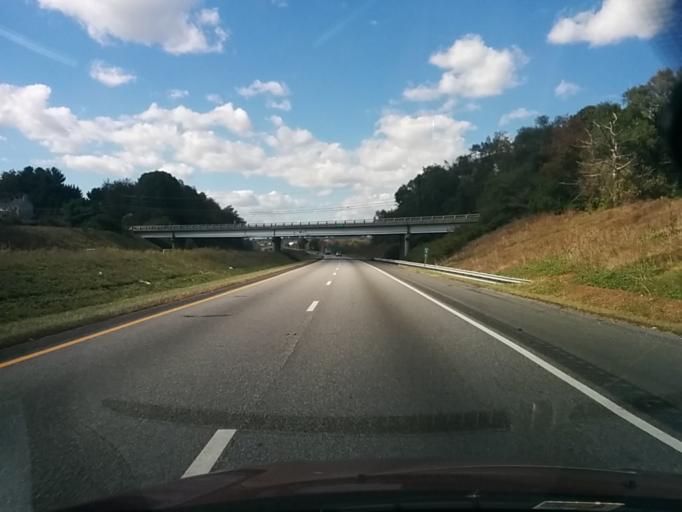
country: US
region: Virginia
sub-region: City of Waynesboro
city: Waynesboro
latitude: 38.0531
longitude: -78.9173
